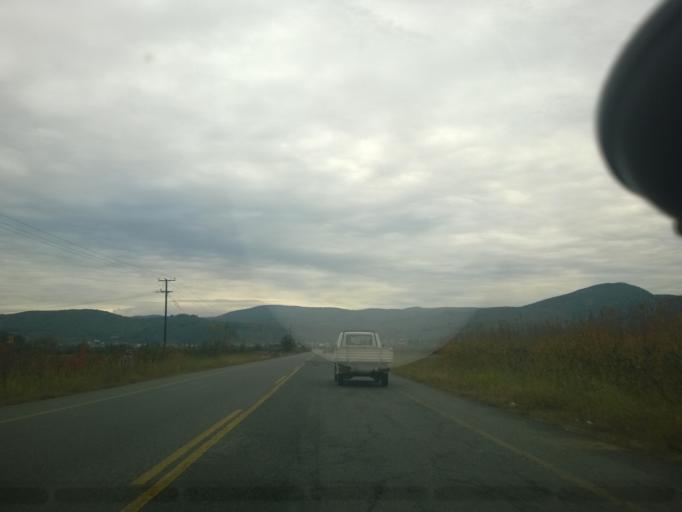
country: GR
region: Central Macedonia
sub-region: Nomos Pellis
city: Apsalos
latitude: 40.9055
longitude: 22.0672
